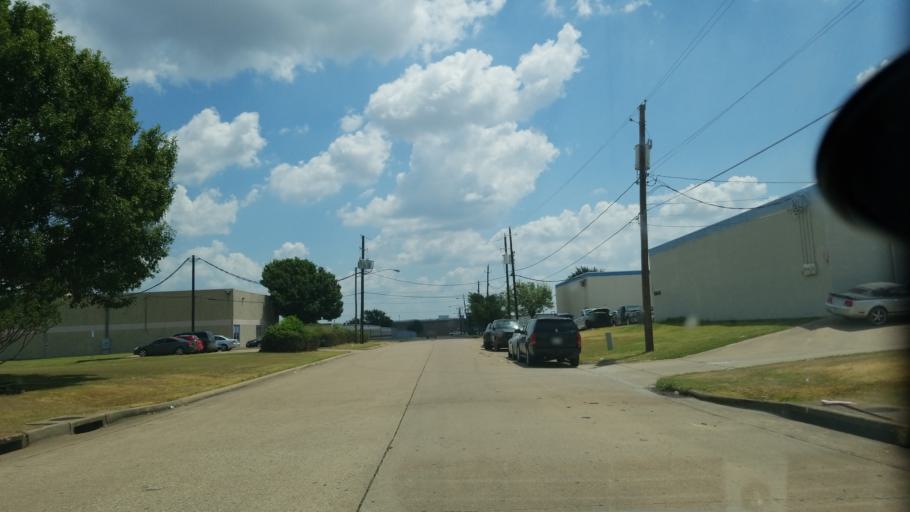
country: US
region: Texas
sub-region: Dallas County
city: Duncanville
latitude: 32.6844
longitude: -96.8946
